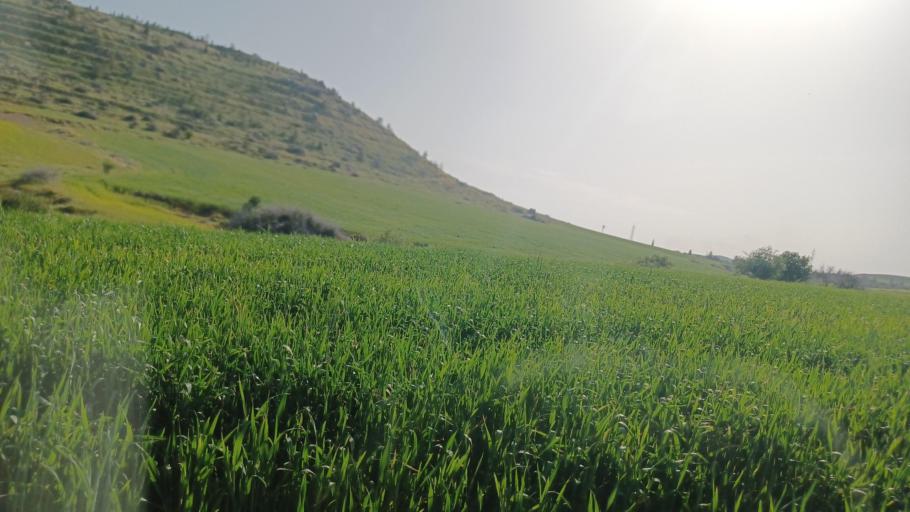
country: CY
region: Lefkosia
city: Astromeritis
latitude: 35.0891
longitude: 32.9520
